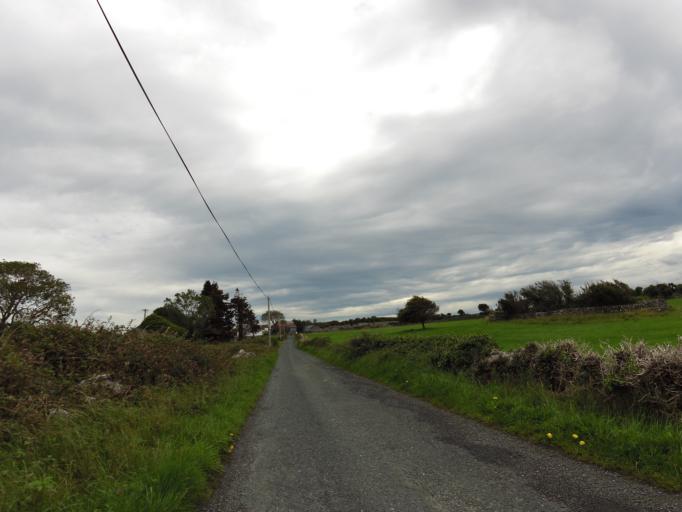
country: IE
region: Connaught
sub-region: County Galway
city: Gaillimh
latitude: 53.3179
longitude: -9.0556
